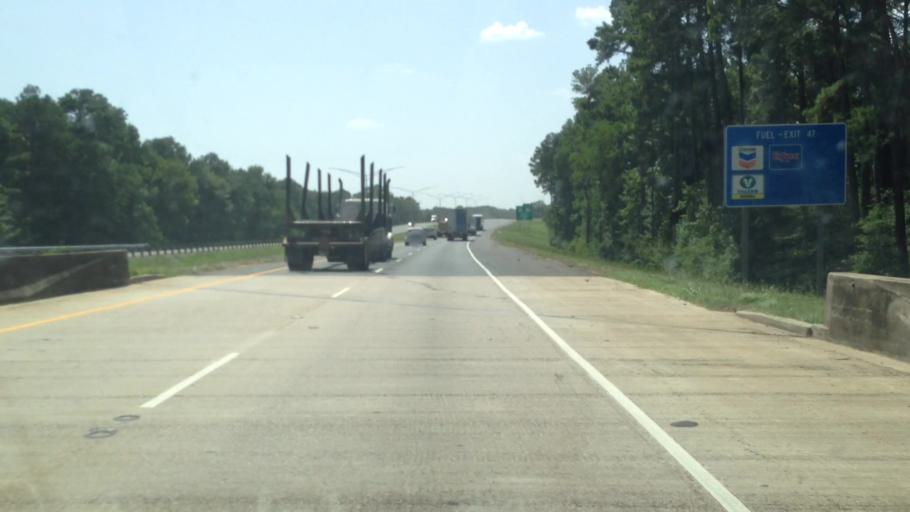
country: US
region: Louisiana
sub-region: Webster Parish
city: Minden
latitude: 32.5881
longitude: -93.2851
